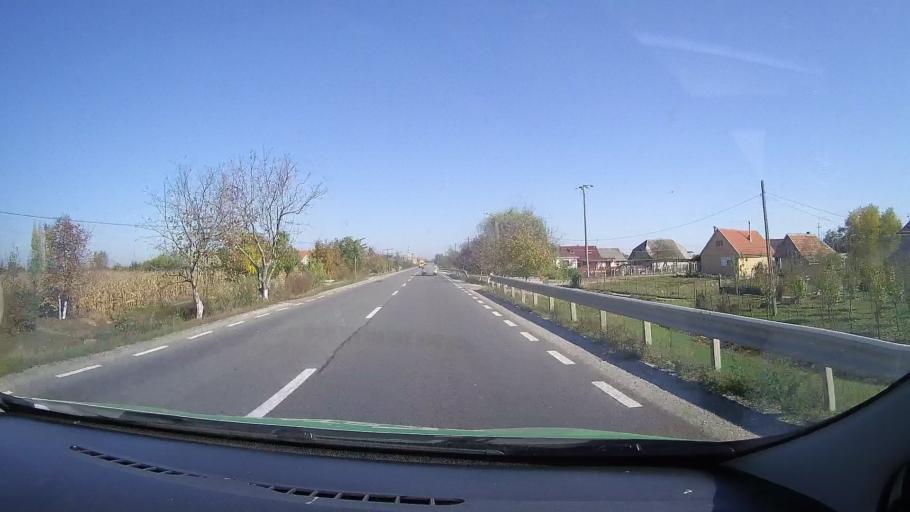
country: RO
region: Satu Mare
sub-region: Comuna Doba
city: Doba
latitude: 47.7368
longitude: 22.7001
